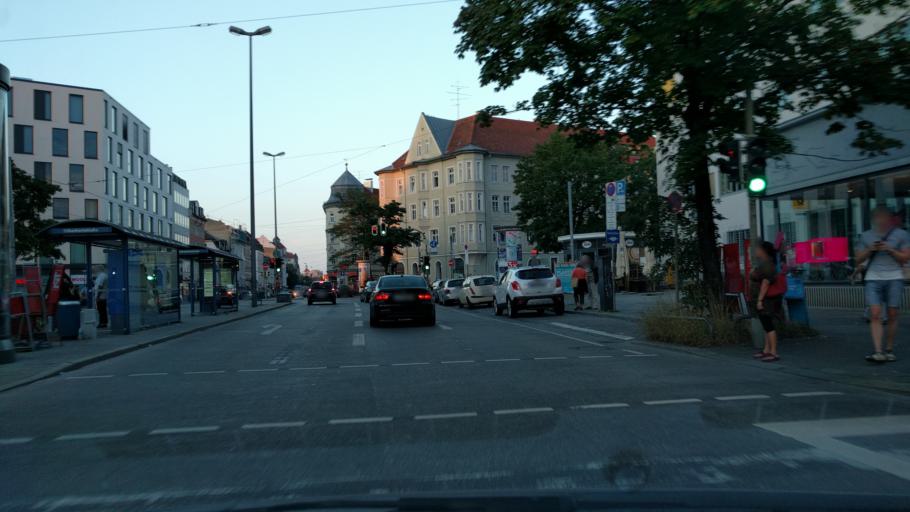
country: DE
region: Bavaria
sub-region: Upper Bavaria
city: Munich
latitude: 48.1152
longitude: 11.5797
